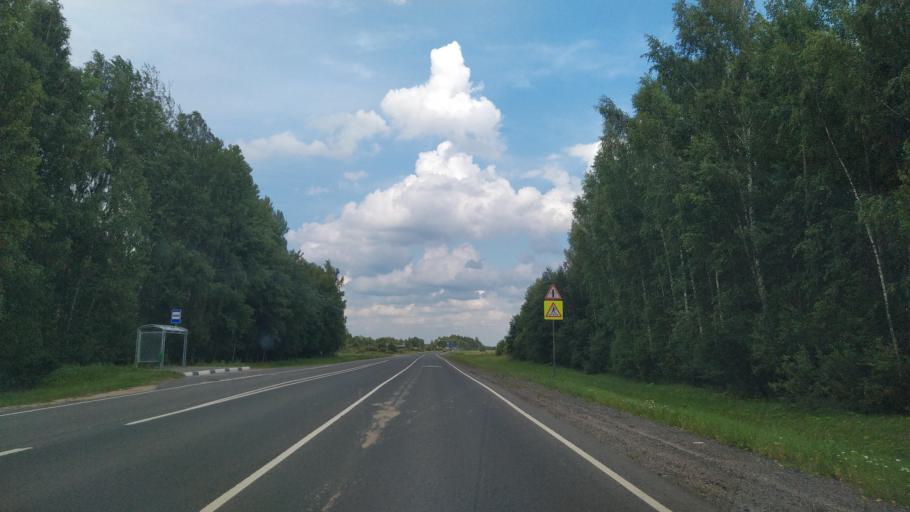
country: RU
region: Novgorod
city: Sol'tsy
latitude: 58.0753
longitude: 30.0654
